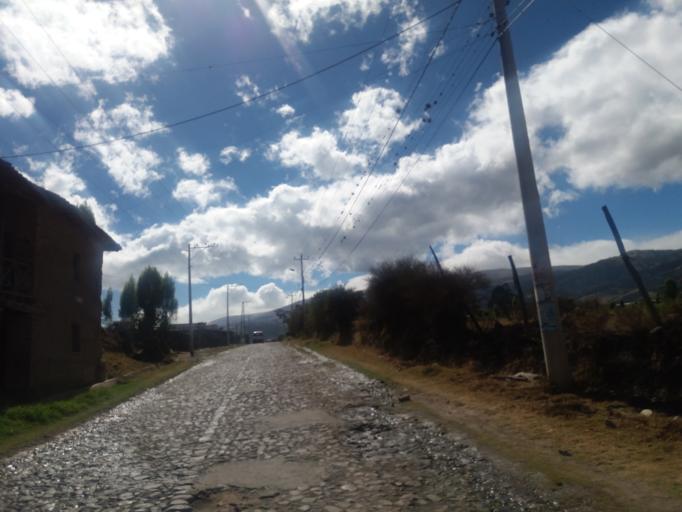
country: EC
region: Pichincha
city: Quito
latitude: -0.1685
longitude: -78.3326
